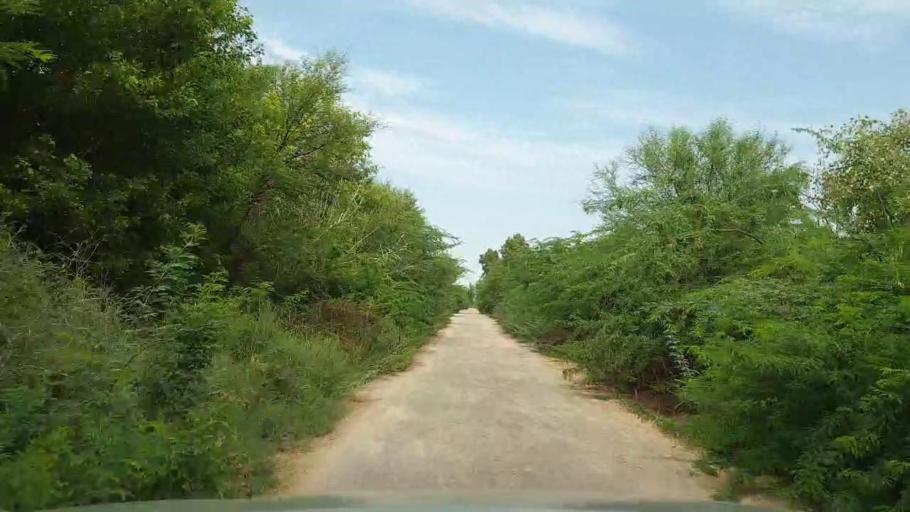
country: PK
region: Sindh
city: Bozdar
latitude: 27.0137
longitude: 68.9405
